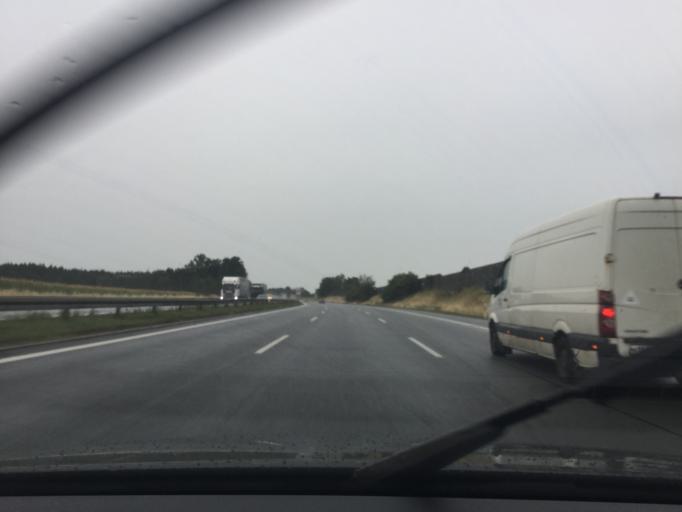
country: DE
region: Saxony
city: Neuensalz
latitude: 50.5296
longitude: 12.2456
